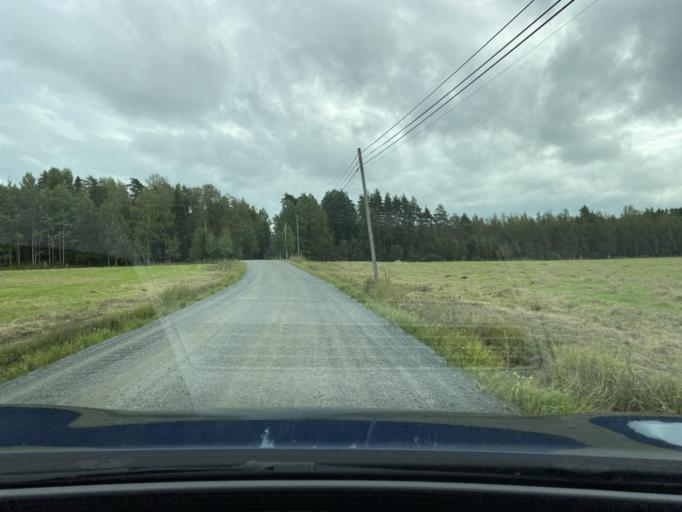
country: FI
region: Pirkanmaa
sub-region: Lounais-Pirkanmaa
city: Vammala
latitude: 61.2663
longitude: 22.9847
